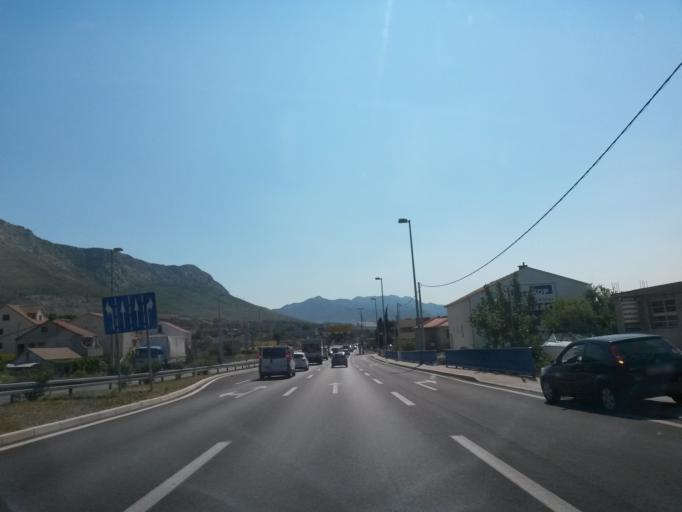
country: HR
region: Splitsko-Dalmatinska
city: Vranjic
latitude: 43.5510
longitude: 16.4270
